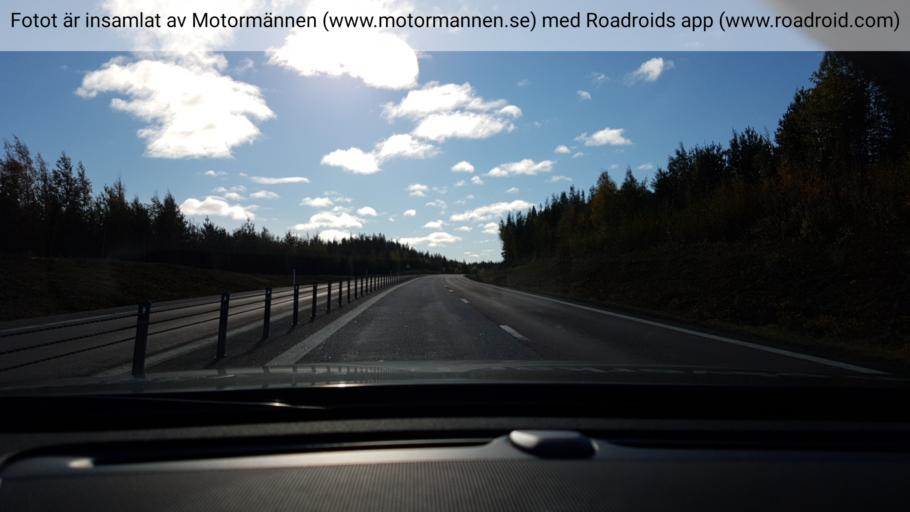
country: SE
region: Vaesterbotten
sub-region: Skelleftea Kommun
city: Skelleftea
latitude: 64.7153
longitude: 20.9924
